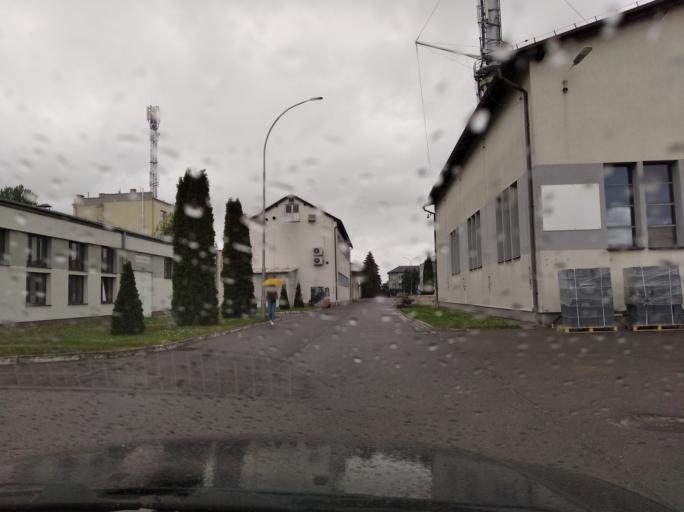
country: PL
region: Subcarpathian Voivodeship
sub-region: Powiat rzeszowski
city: Boguchwala
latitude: 49.9865
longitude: 21.9345
